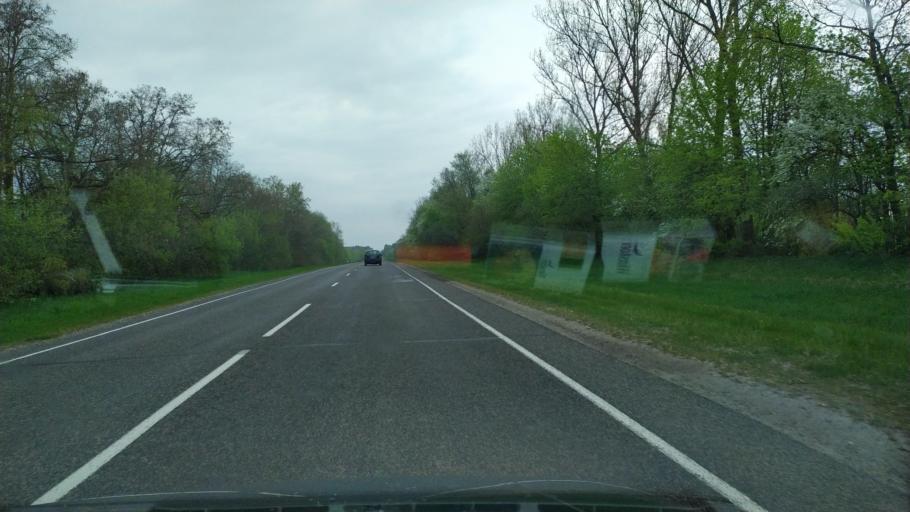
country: BY
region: Brest
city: Horad Kobryn
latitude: 52.2929
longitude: 24.5045
